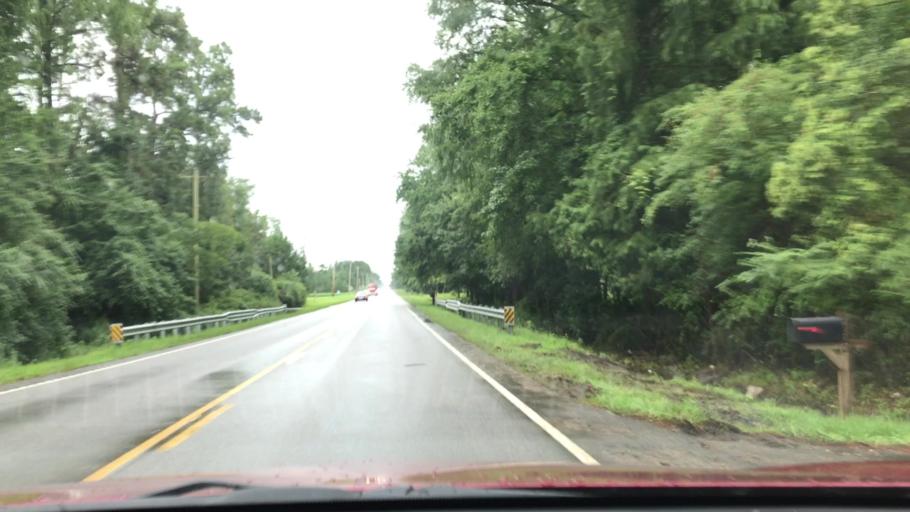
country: US
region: South Carolina
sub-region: Horry County
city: Conway
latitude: 33.7690
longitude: -79.0723
